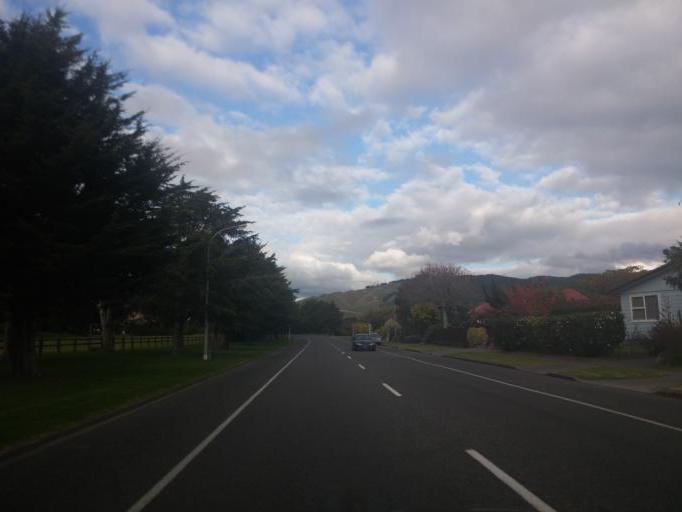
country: NZ
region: Wellington
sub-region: Kapiti Coast District
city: Paraparaumu
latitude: -40.8725
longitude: 175.0456
